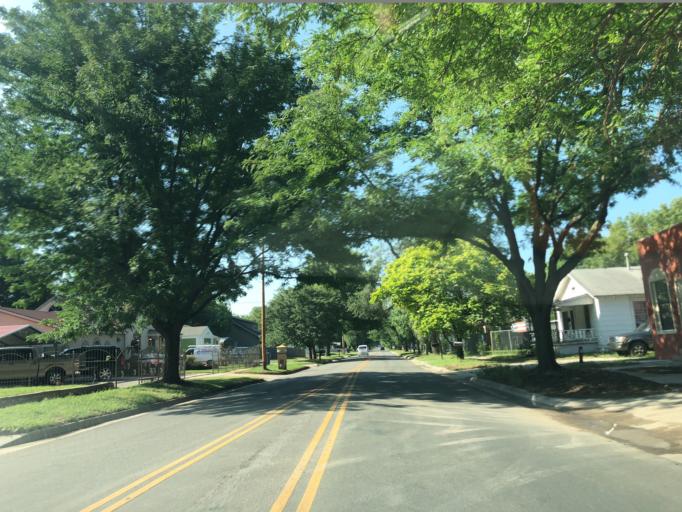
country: US
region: Kansas
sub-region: Sedgwick County
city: Wichita
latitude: 37.7293
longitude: -97.3448
